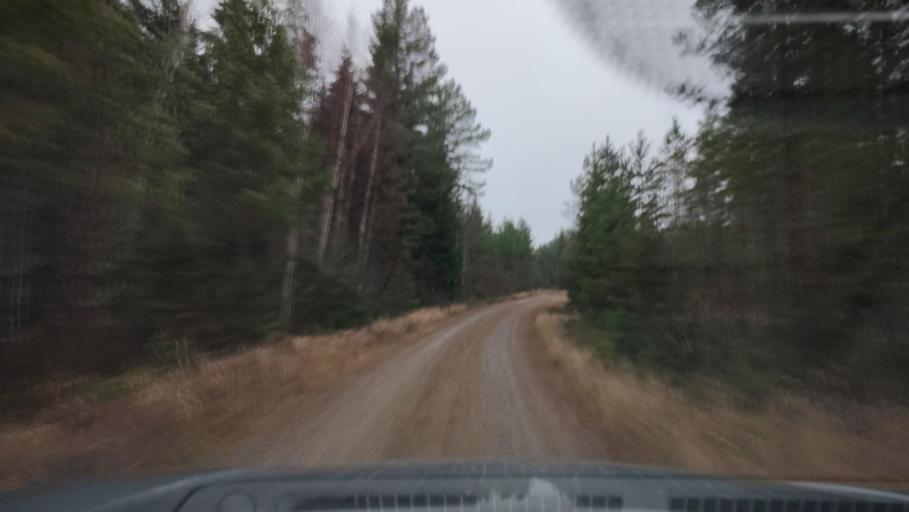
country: FI
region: Southern Ostrobothnia
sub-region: Suupohja
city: Karijoki
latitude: 62.1571
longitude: 21.5895
